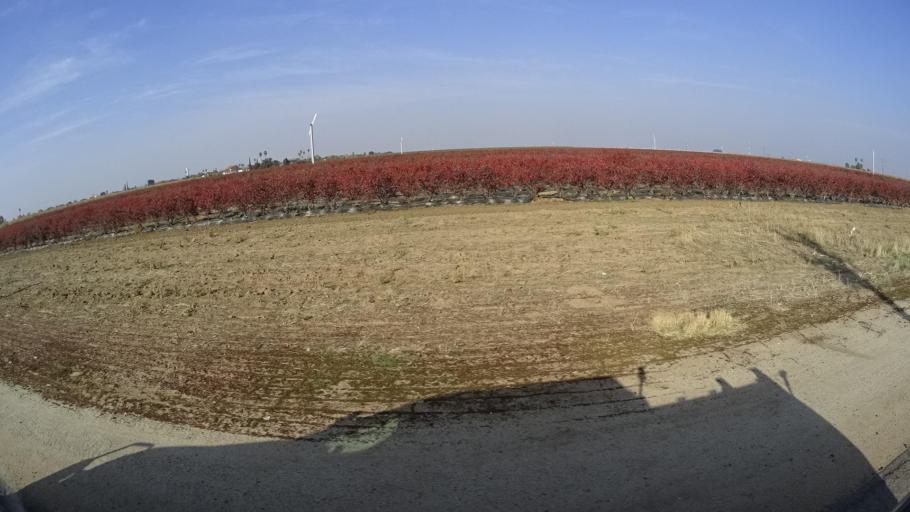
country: US
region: California
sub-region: Tulare County
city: Richgrove
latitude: 35.7907
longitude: -119.1008
